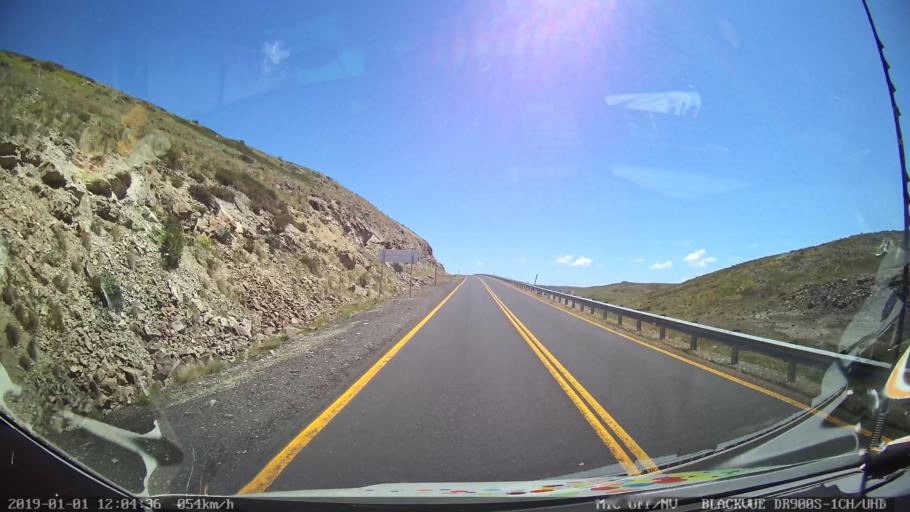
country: AU
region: New South Wales
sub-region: Snowy River
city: Jindabyne
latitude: -35.8655
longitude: 148.4967
